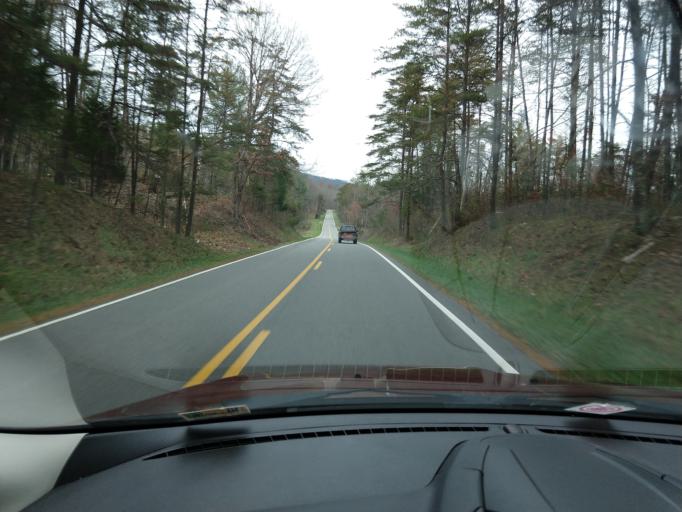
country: US
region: Virginia
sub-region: City of Covington
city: Covington
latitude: 37.7750
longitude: -80.1098
